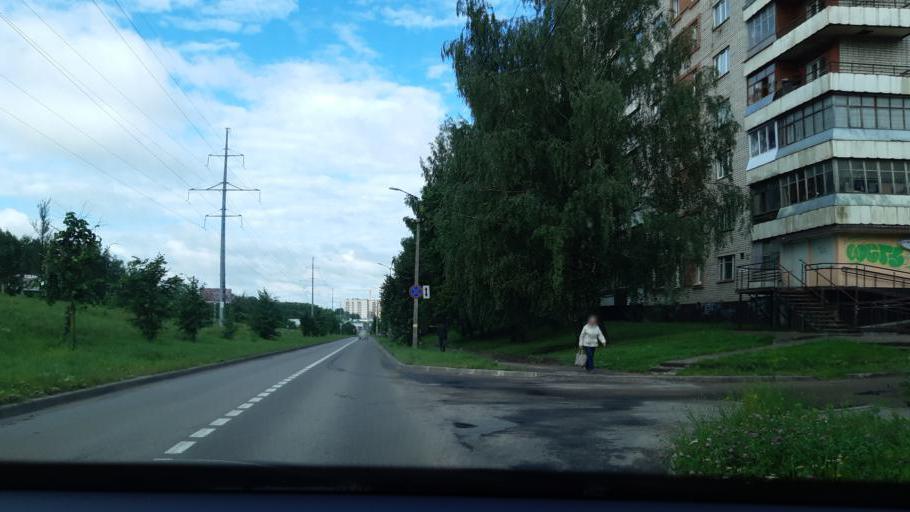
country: RU
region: Smolensk
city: Smolensk
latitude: 54.7645
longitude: 32.0900
